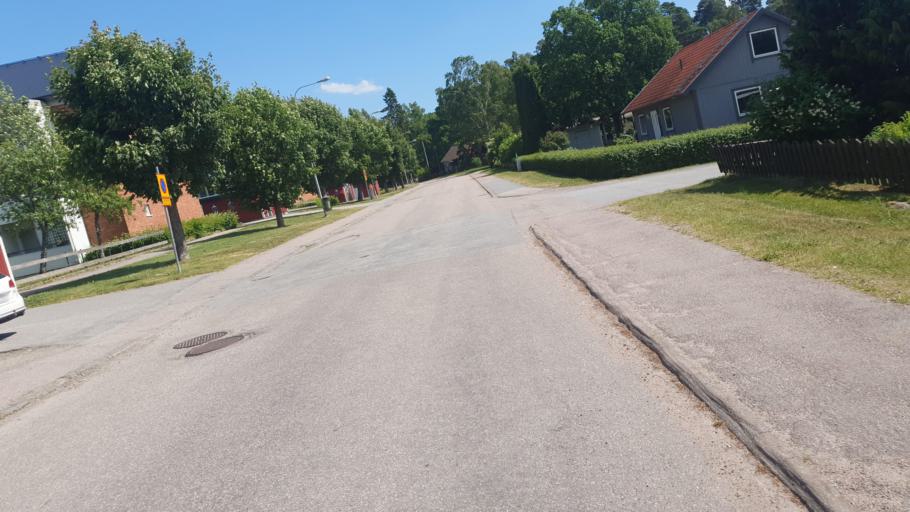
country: SE
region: Uppsala
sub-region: Osthammars Kommun
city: Gimo
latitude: 60.1720
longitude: 18.1758
